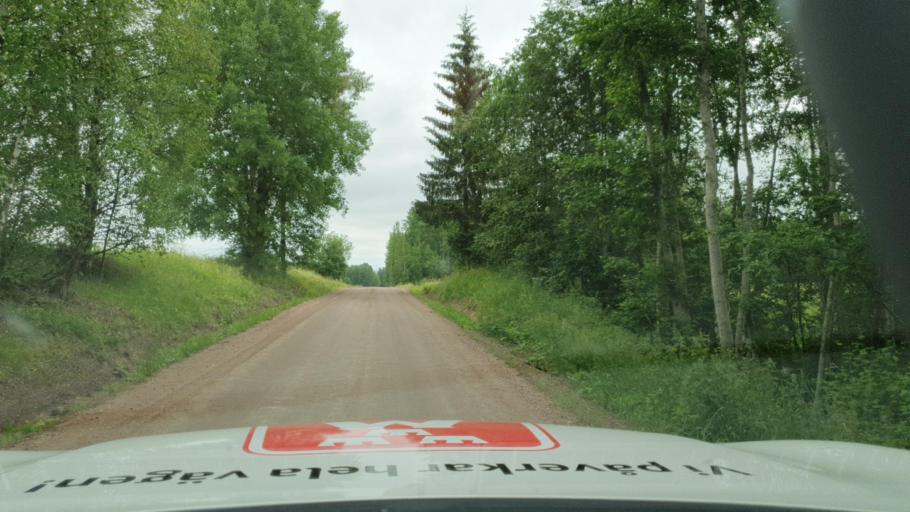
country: SE
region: Vaermland
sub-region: Filipstads Kommun
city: Filipstad
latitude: 59.5444
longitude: 13.9733
